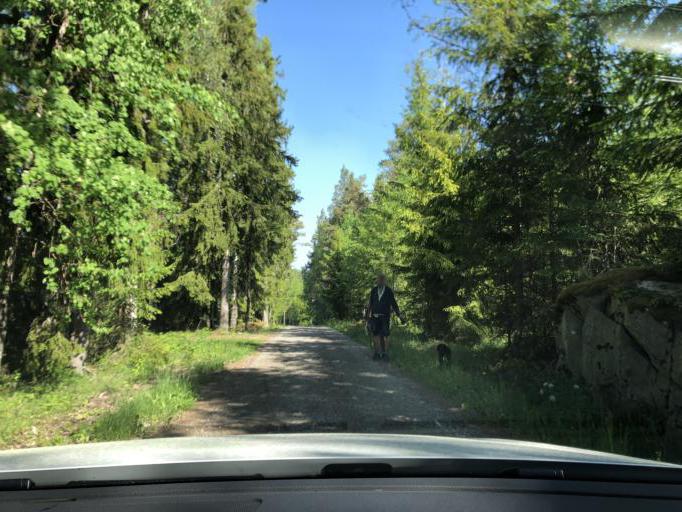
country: SE
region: Dalarna
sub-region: Avesta Kommun
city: Horndal
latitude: 60.2040
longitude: 16.4971
